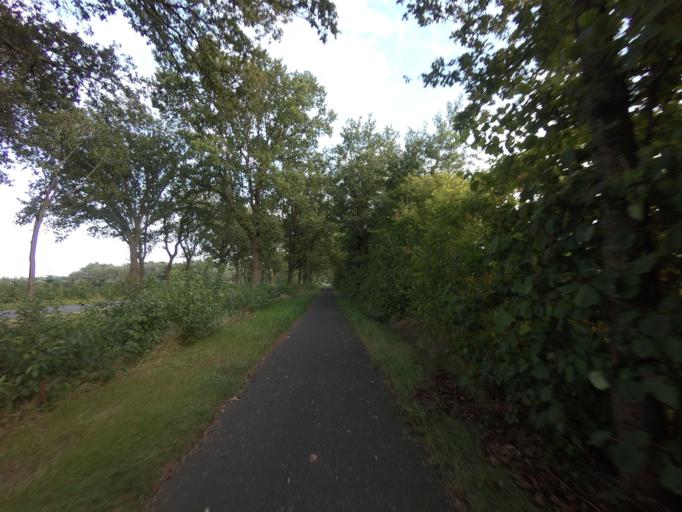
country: DE
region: Lower Saxony
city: Wielen
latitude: 52.5484
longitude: 6.6899
